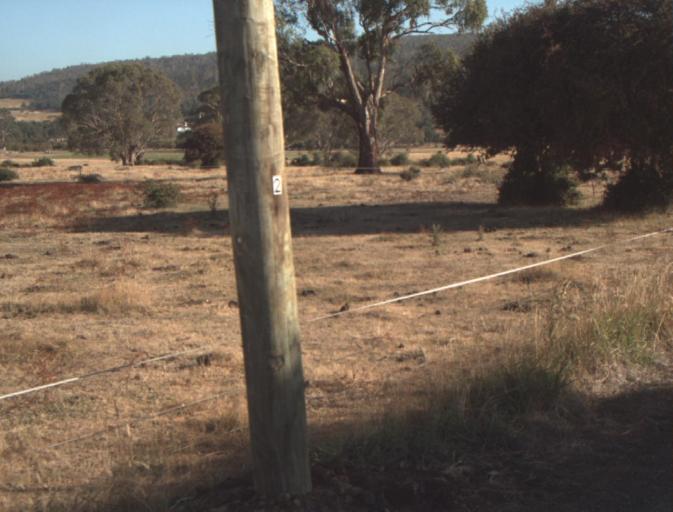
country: AU
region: Tasmania
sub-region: Launceston
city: Newstead
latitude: -41.4369
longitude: 147.2110
